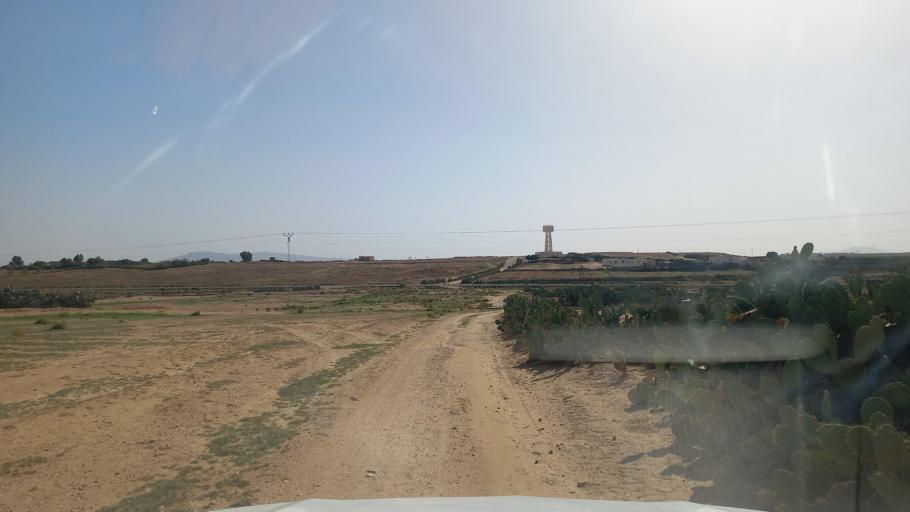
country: TN
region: Al Qasrayn
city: Sbiba
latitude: 35.3160
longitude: 9.0233
